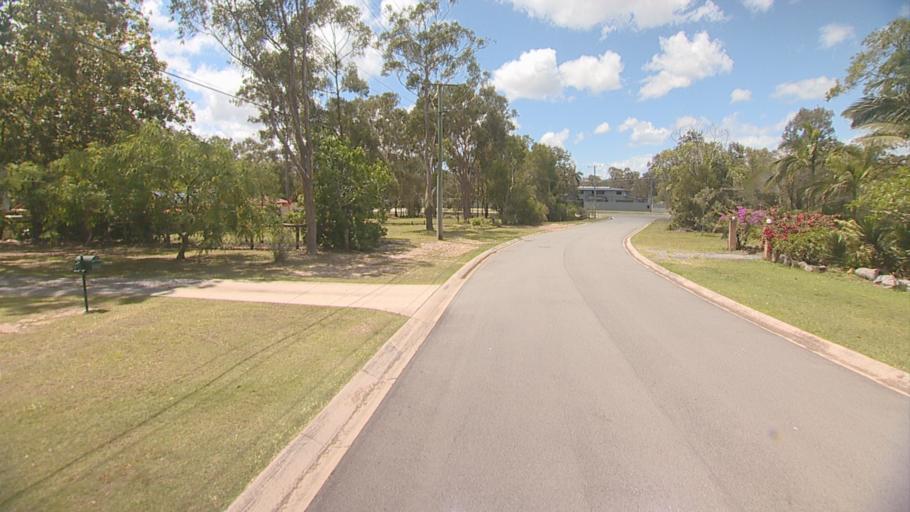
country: AU
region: Queensland
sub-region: Logan
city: Beenleigh
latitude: -27.6669
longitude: 153.2171
